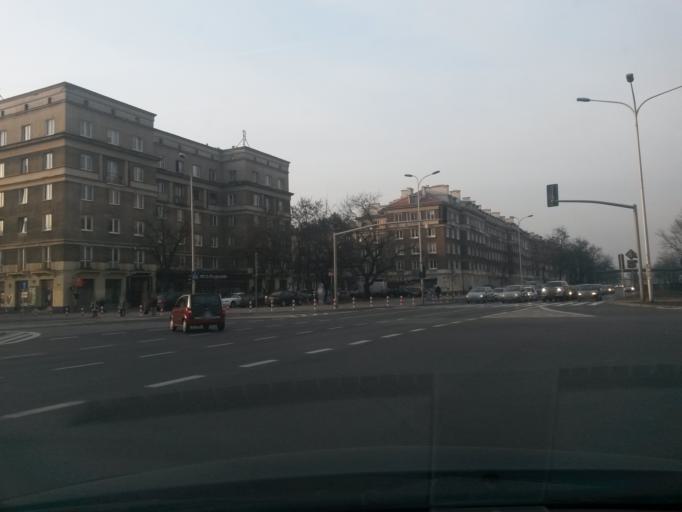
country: PL
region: Masovian Voivodeship
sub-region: Warszawa
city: Mokotow
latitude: 52.2070
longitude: 21.0485
